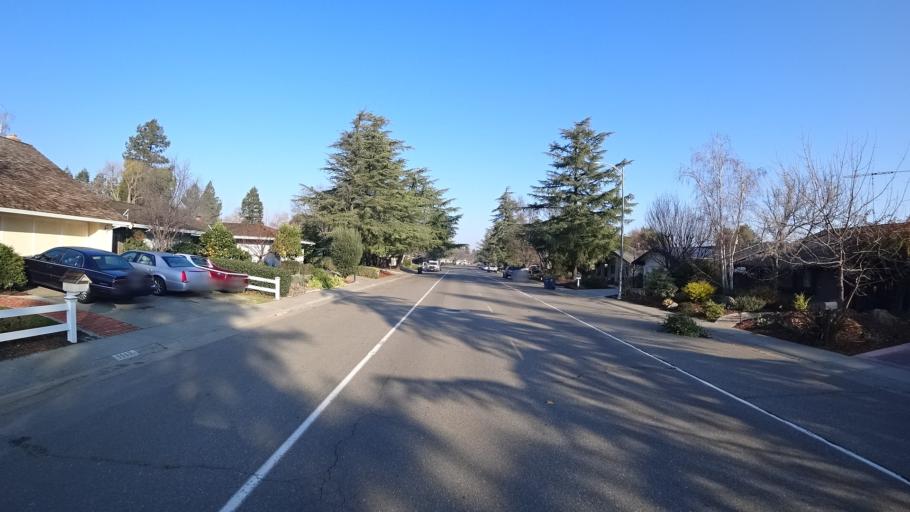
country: US
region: California
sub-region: Yolo County
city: Davis
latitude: 38.5536
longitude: -121.7918
